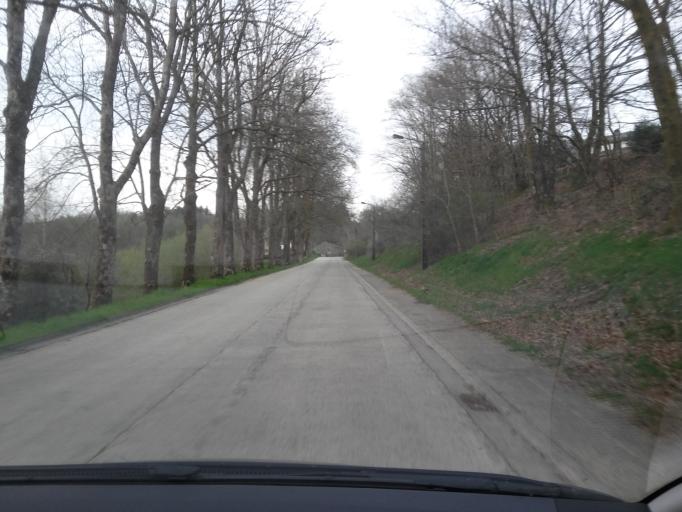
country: BE
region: Wallonia
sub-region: Province du Luxembourg
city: Herbeumont
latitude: 49.7831
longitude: 5.2434
